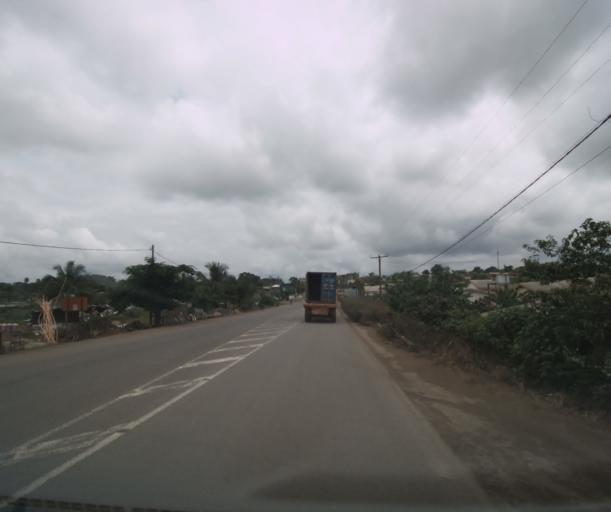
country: CM
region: Littoral
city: Edea
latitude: 3.7883
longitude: 10.1428
